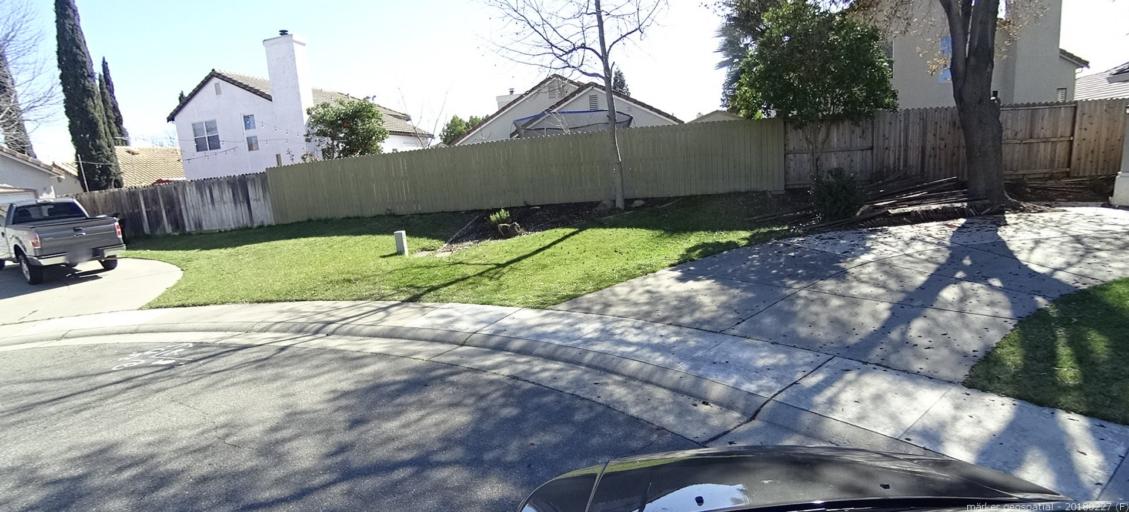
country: US
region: California
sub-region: Sacramento County
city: North Highlands
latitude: 38.7266
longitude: -121.3782
